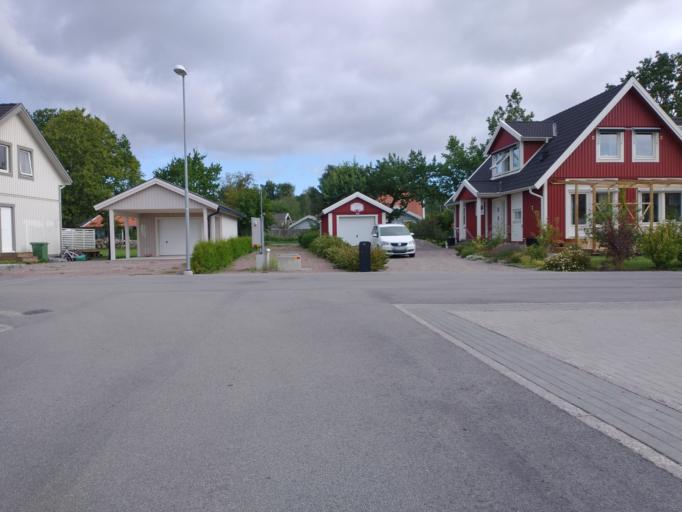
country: SE
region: Kalmar
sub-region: Kalmar Kommun
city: Lindsdal
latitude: 56.7793
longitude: 16.3020
